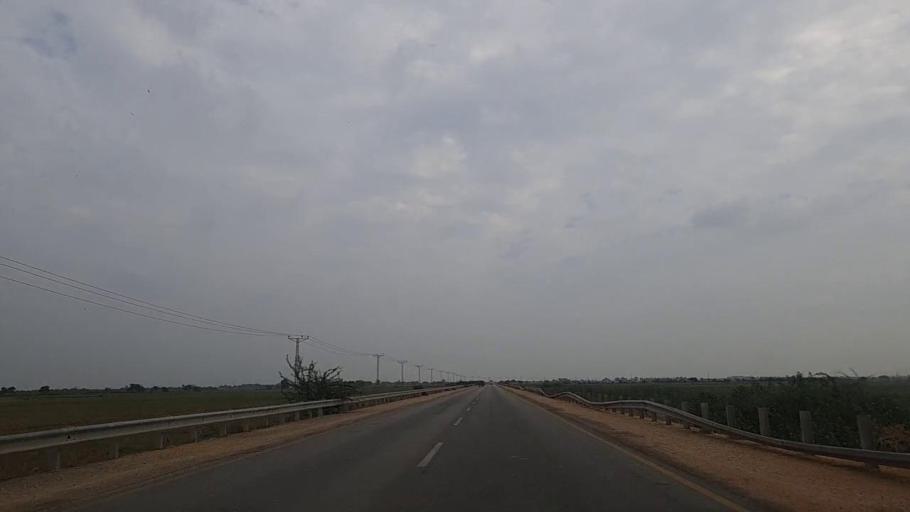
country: PK
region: Sindh
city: Thatta
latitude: 24.6170
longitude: 68.0676
